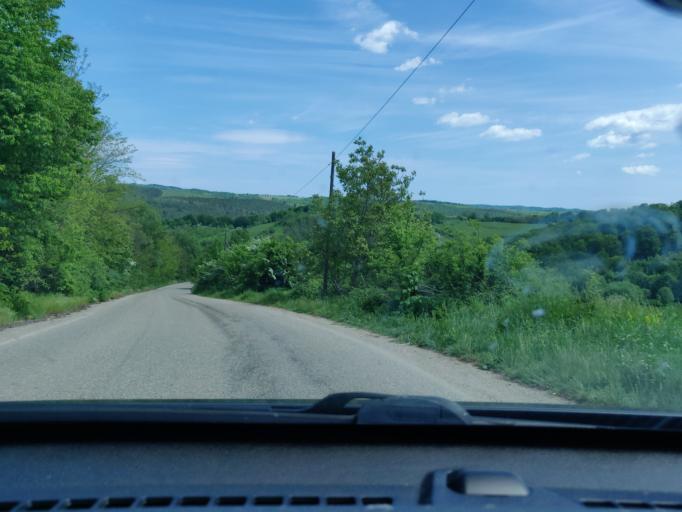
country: RO
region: Vrancea
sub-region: Comuna Campuri
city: Campuri
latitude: 45.9992
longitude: 26.7909
